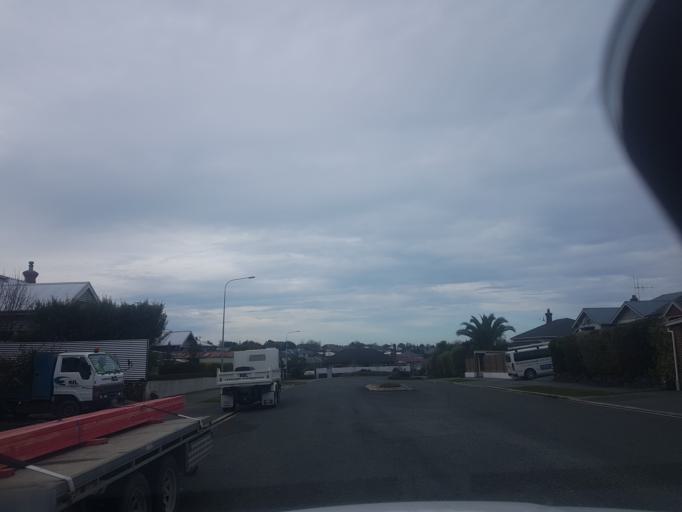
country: NZ
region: Canterbury
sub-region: Timaru District
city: Timaru
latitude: -44.4039
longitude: 171.2331
